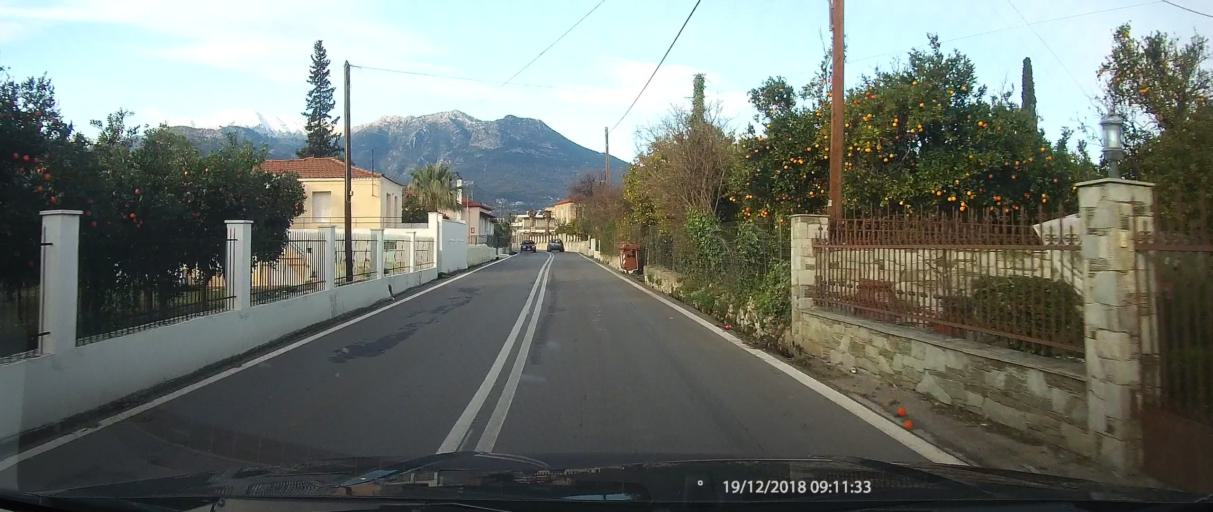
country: GR
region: Peloponnese
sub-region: Nomos Lakonias
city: Magoula
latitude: 37.0788
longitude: 22.4139
